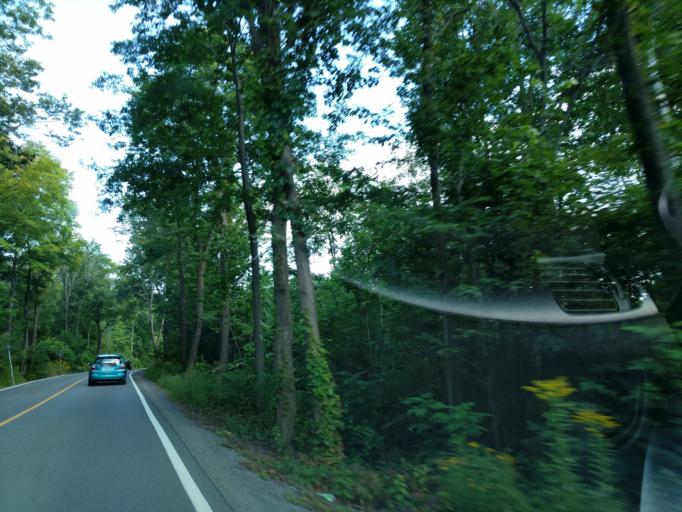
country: CA
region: Quebec
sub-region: Outaouais
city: Gatineau
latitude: 45.4507
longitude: -75.7888
